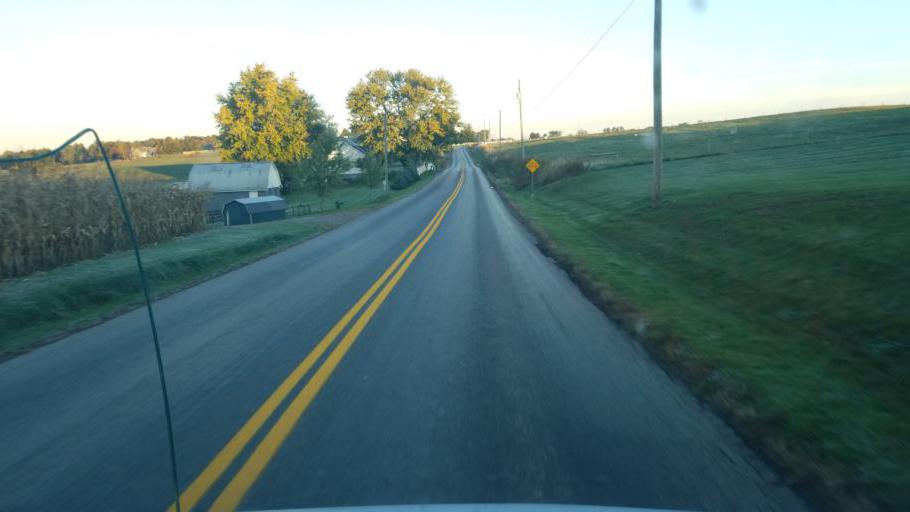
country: US
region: Ohio
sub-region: Stark County
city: Brewster
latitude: 40.6639
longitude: -81.7016
